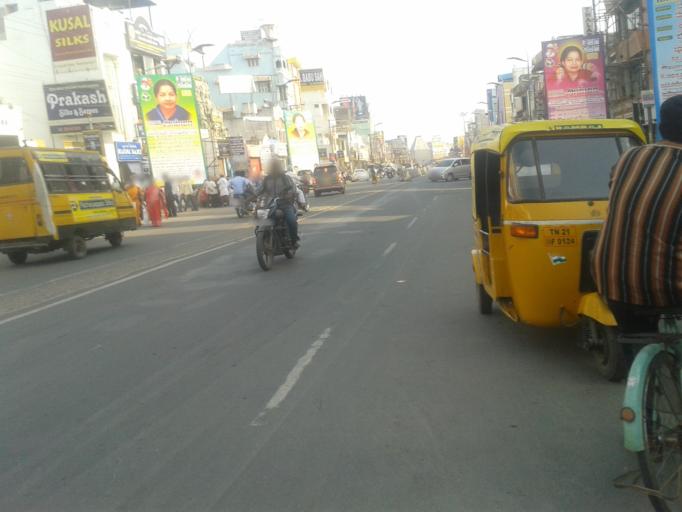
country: IN
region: Tamil Nadu
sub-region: Kancheepuram
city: Kanchipuram
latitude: 12.8284
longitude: 79.7072
